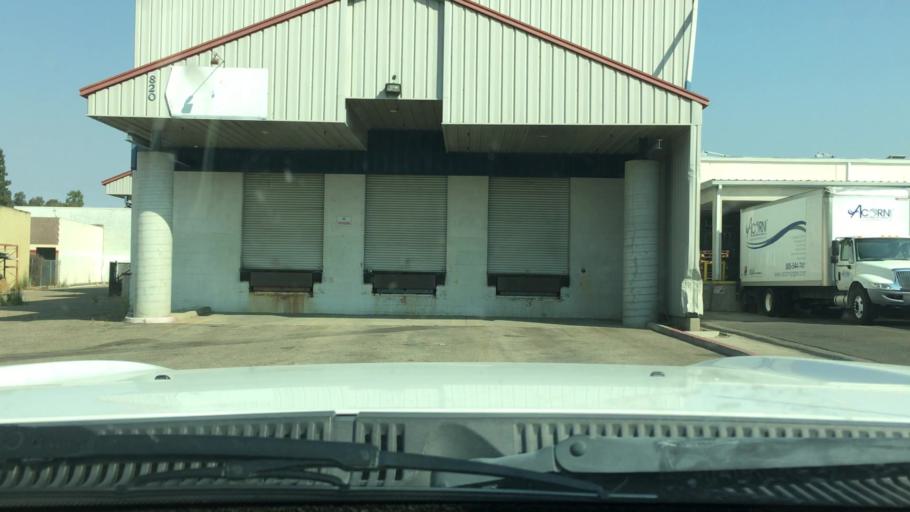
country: US
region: California
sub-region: San Luis Obispo County
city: San Luis Obispo
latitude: 35.2576
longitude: -120.6440
